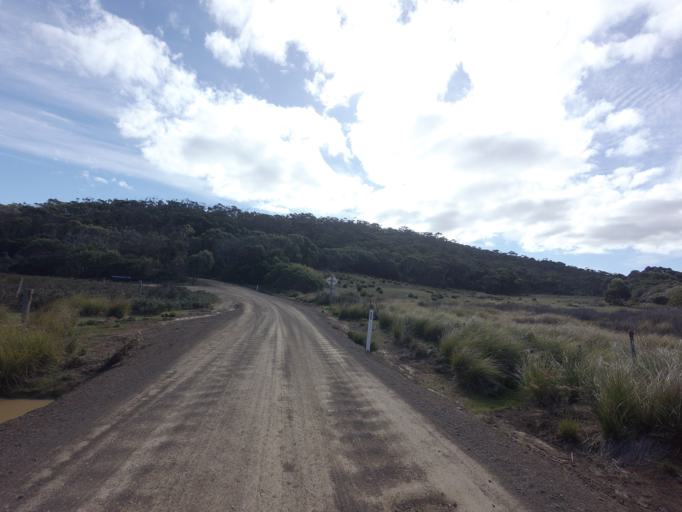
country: AU
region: Tasmania
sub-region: Clarence
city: Sandford
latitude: -43.0838
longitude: 147.6787
